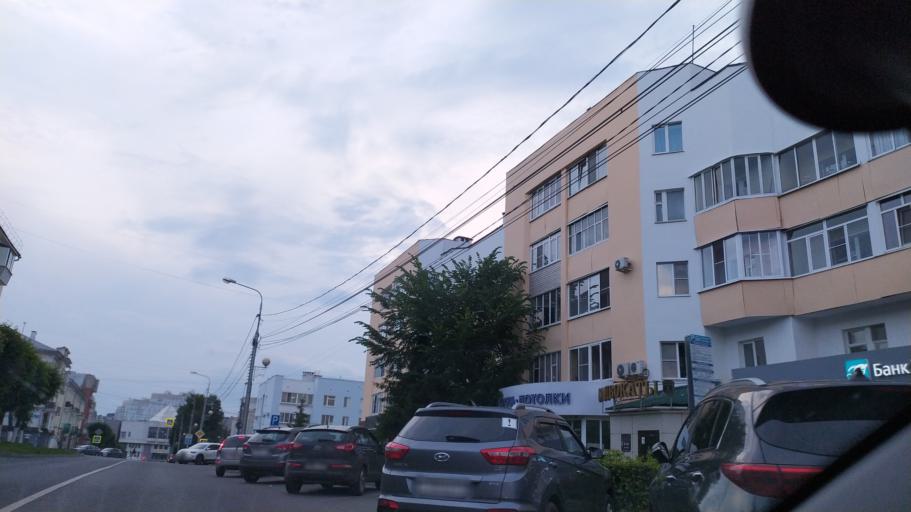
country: RU
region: Chuvashia
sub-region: Cheboksarskiy Rayon
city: Cheboksary
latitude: 56.1418
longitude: 47.2493
